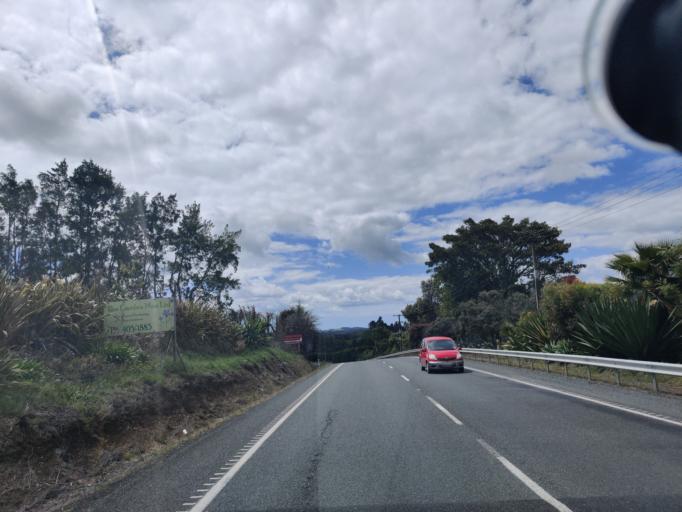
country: NZ
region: Northland
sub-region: Far North District
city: Kerikeri
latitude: -35.2395
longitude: 173.9189
